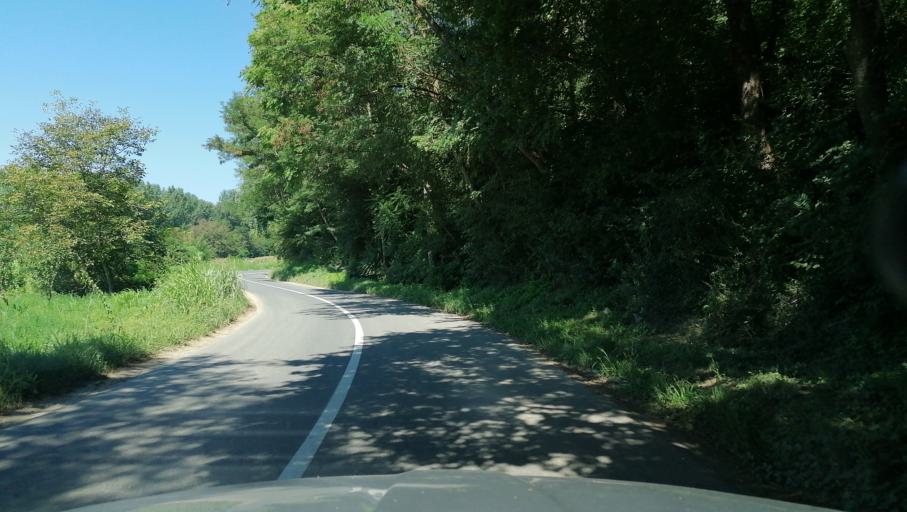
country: RS
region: Central Serbia
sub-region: Raski Okrug
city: Vrnjacka Banja
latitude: 43.6612
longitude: 20.9273
